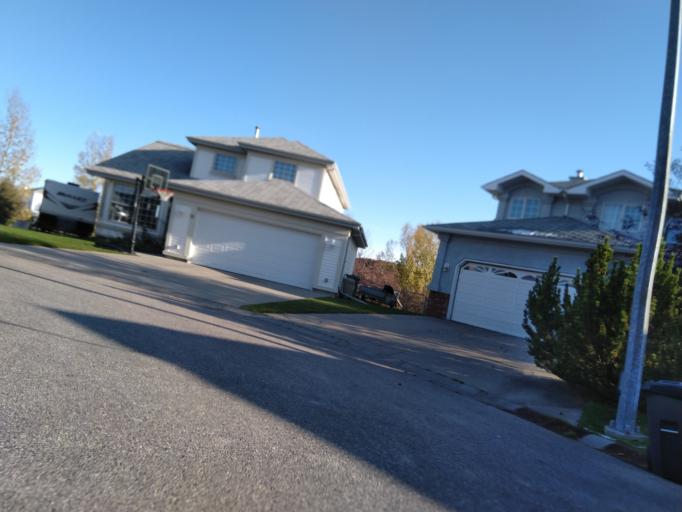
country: CA
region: Alberta
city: Cochrane
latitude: 51.1762
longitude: -114.4715
